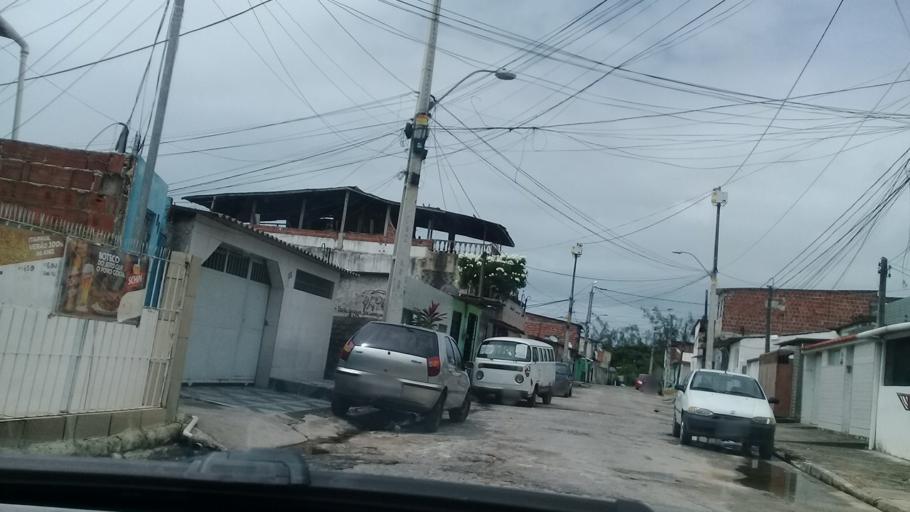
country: BR
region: Pernambuco
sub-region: Jaboatao Dos Guararapes
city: Jaboatao dos Guararapes
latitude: -8.1157
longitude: -34.9458
